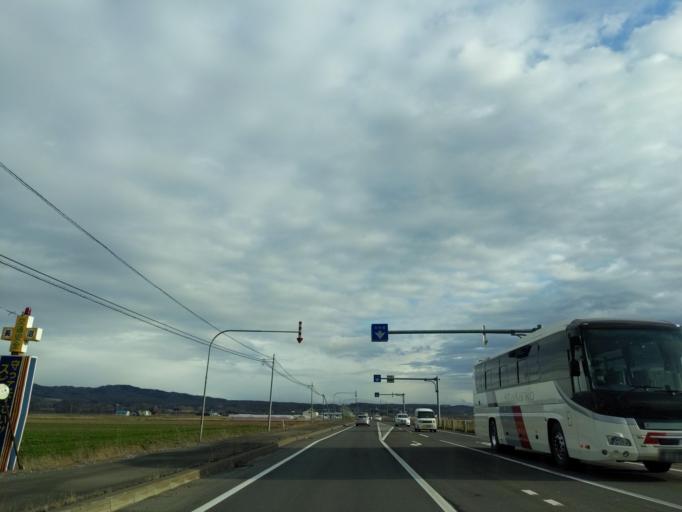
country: JP
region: Hokkaido
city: Kitahiroshima
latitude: 42.9579
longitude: 141.6961
